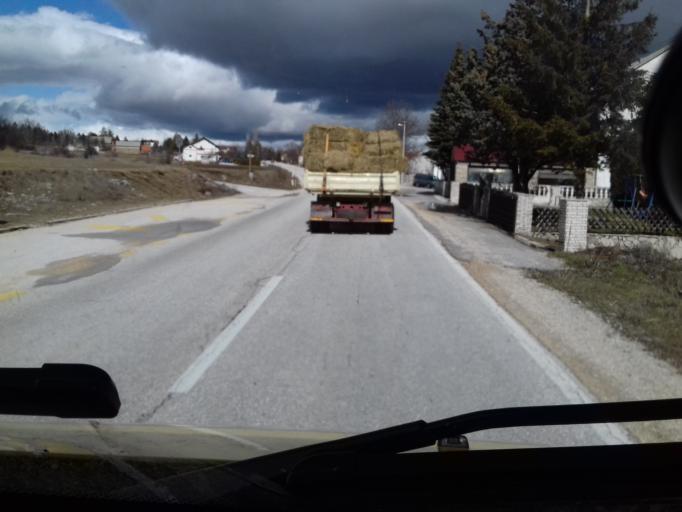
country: BA
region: Federation of Bosnia and Herzegovina
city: Dreznica
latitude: 43.6022
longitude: 17.2735
